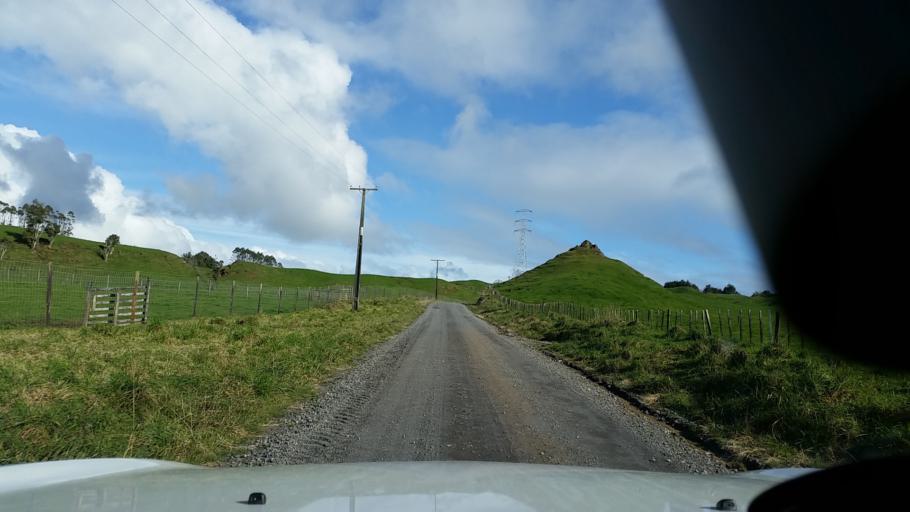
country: NZ
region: Bay of Plenty
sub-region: Rotorua District
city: Rotorua
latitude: -38.0052
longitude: 176.2016
